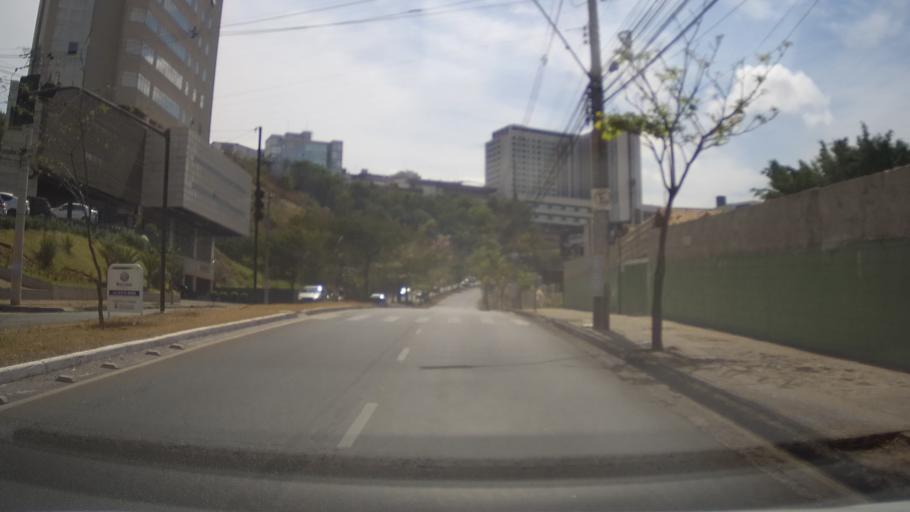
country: BR
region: Minas Gerais
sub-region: Belo Horizonte
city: Belo Horizonte
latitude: -19.9650
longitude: -43.9591
